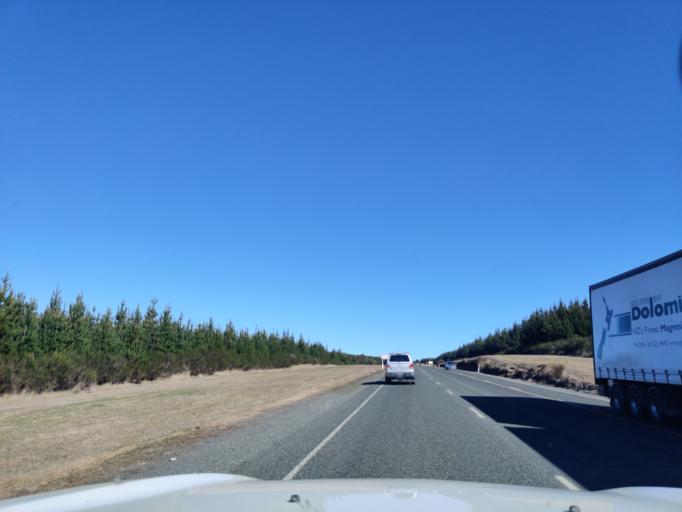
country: NZ
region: Waikato
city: Turangi
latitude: -39.1242
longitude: 175.7956
